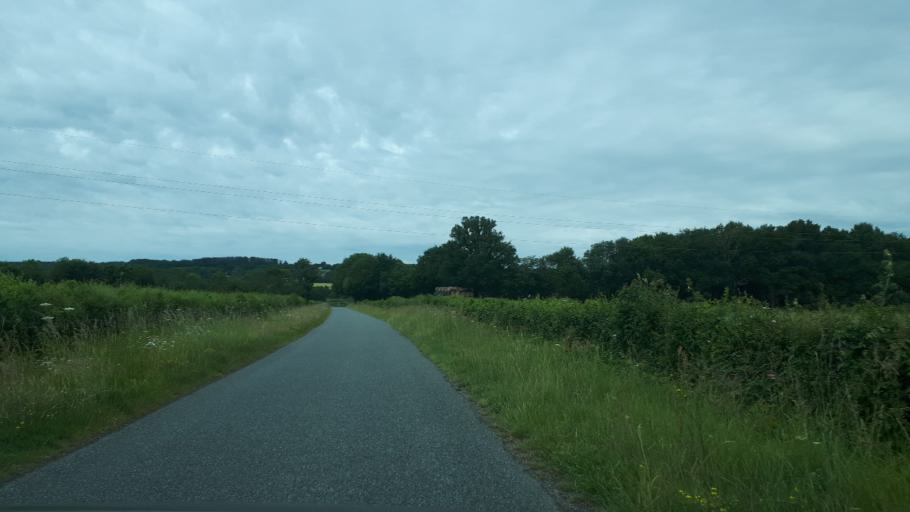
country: FR
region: Centre
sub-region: Departement du Cher
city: Henrichemont
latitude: 47.4106
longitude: 2.6317
